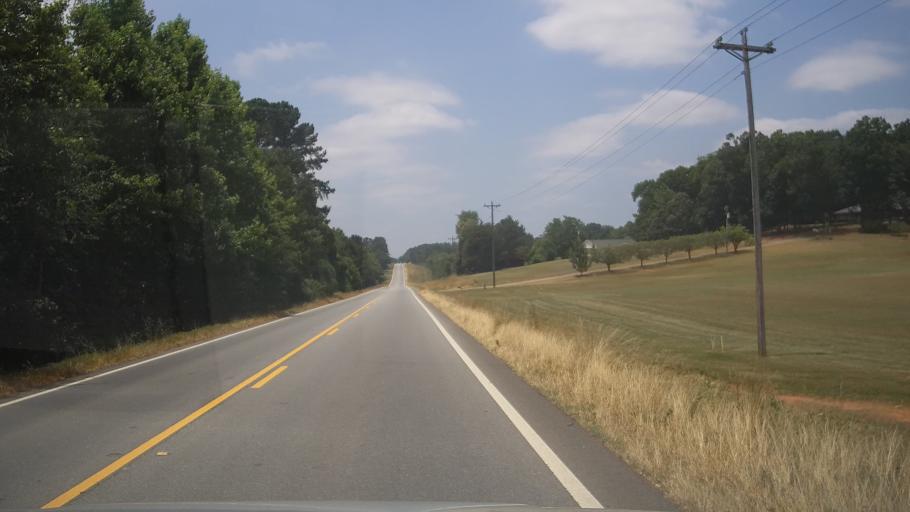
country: US
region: Georgia
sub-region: Jackson County
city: Nicholson
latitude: 34.1783
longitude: -83.3755
